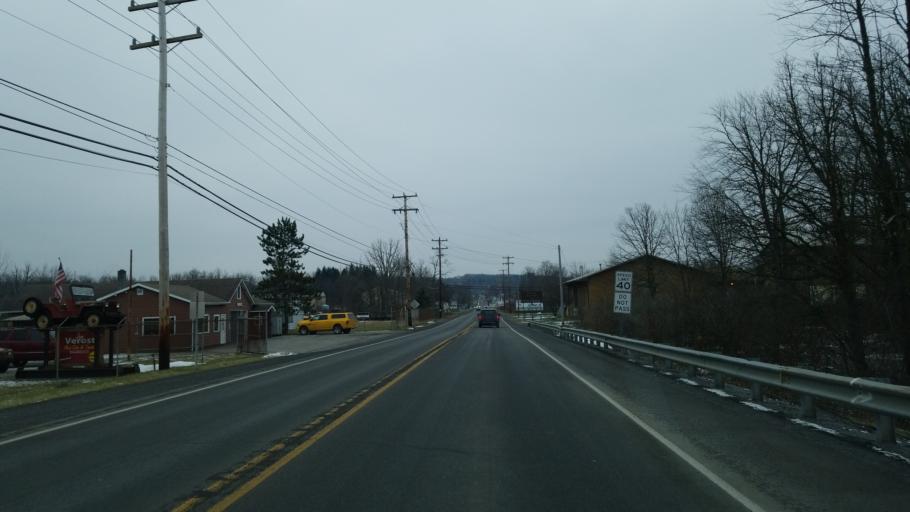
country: US
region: Pennsylvania
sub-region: Clearfield County
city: Troy
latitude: 40.9088
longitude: -78.2239
